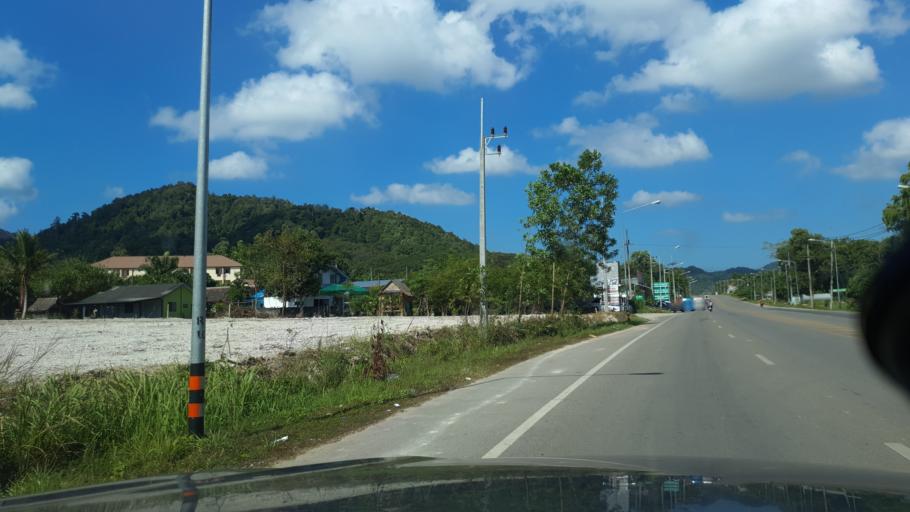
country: TH
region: Phangnga
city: Ban Ao Nang
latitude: 8.0349
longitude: 98.8579
